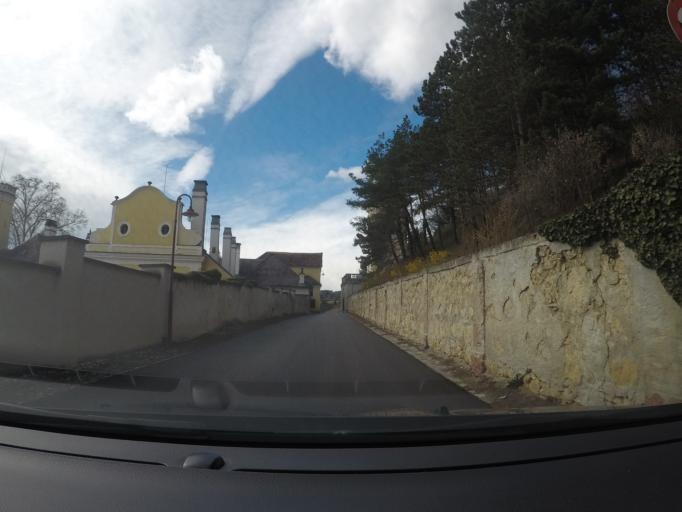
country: AT
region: Lower Austria
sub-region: Politischer Bezirk Wiener Neustadt
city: Bad Erlach
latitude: 47.7279
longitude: 16.1993
